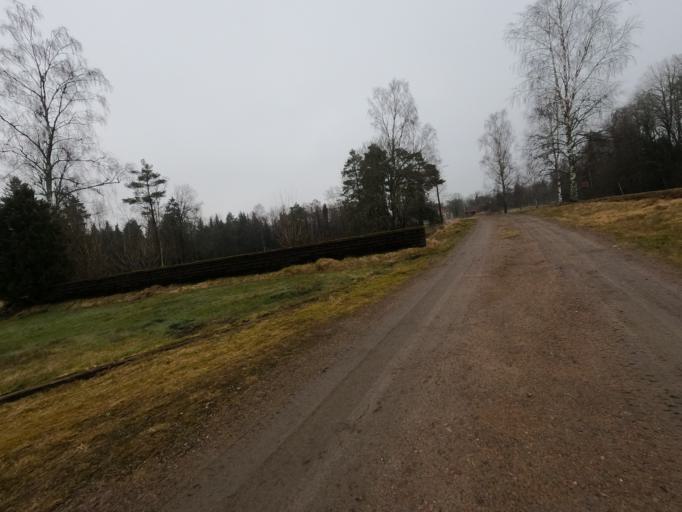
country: SE
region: Halland
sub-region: Hylte Kommun
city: Hyltebruk
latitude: 56.8076
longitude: 13.2661
